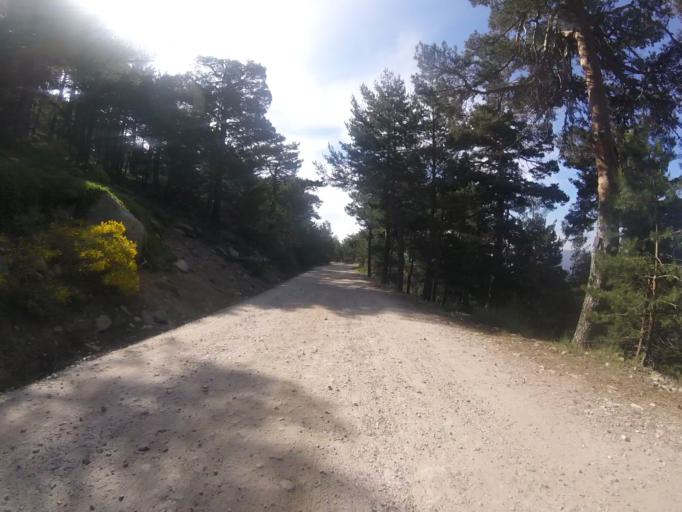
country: ES
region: Madrid
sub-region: Provincia de Madrid
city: Guadarrama
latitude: 40.6868
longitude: -4.1626
